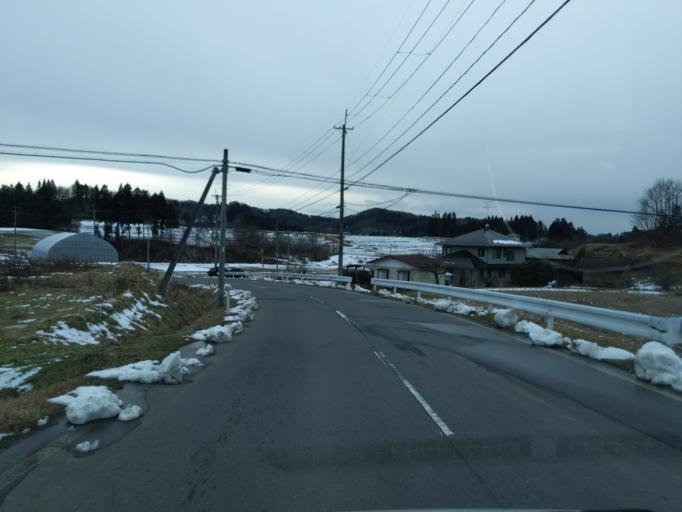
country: JP
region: Iwate
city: Mizusawa
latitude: 39.1830
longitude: 141.2451
